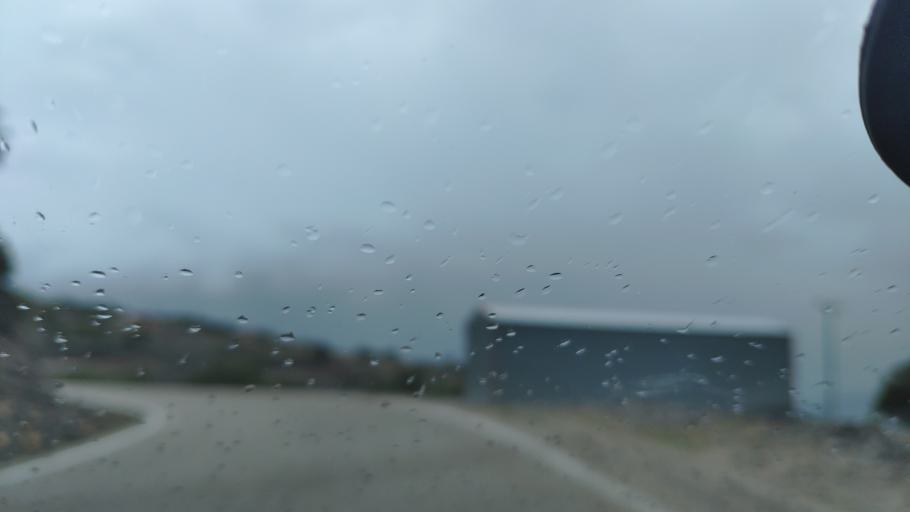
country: GR
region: West Greece
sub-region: Nomos Aitolias kai Akarnanias
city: Krikellos
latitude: 39.0745
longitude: 21.3891
